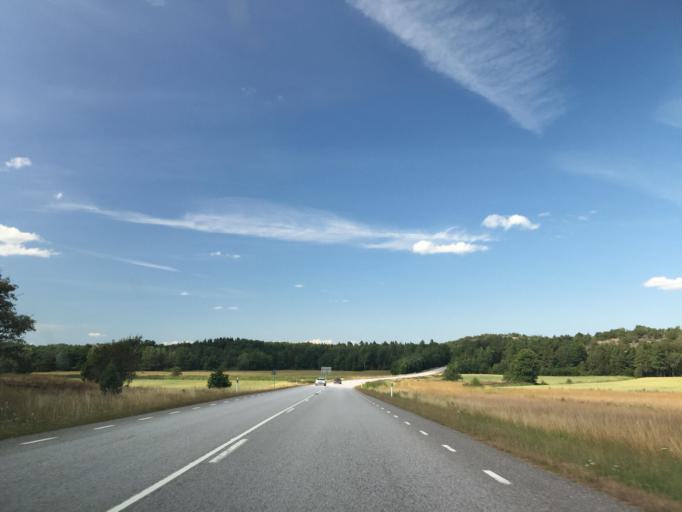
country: SE
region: Vaestra Goetaland
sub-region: Tanums Kommun
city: Tanumshede
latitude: 58.8123
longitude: 11.2635
